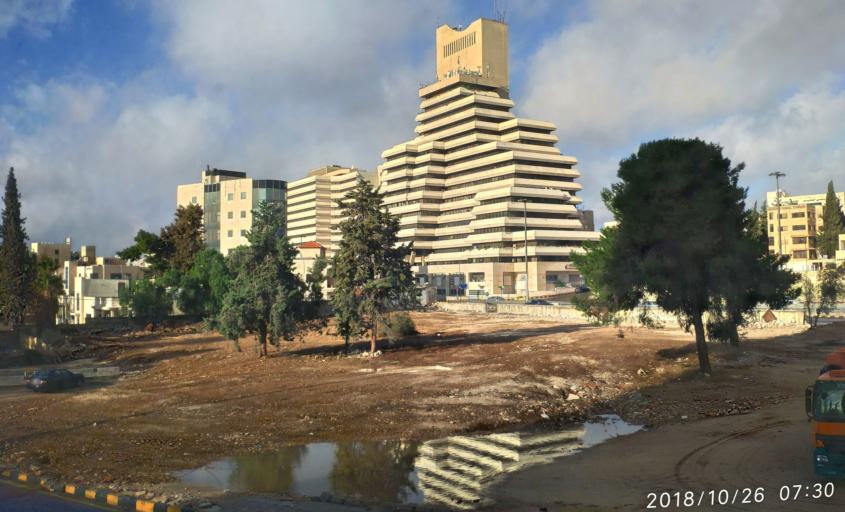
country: JO
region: Amman
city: Amman
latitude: 31.9718
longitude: 35.9095
